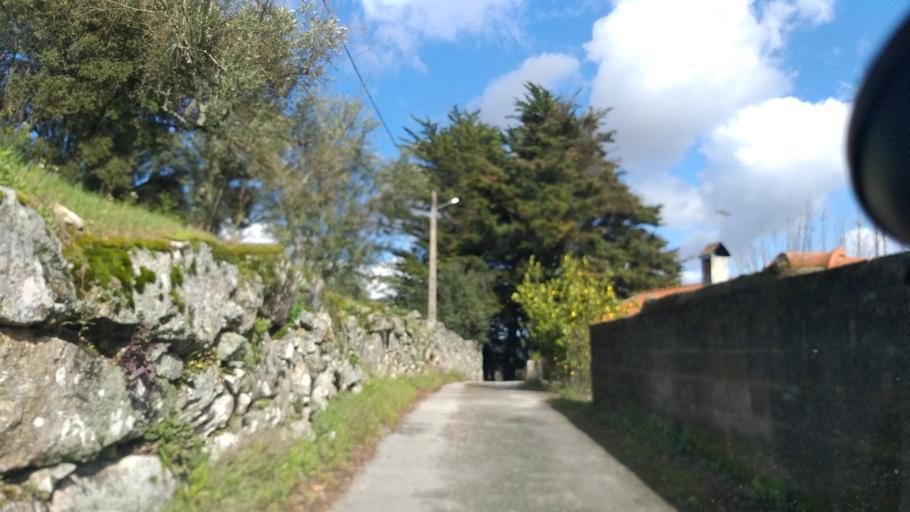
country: PT
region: Guarda
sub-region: Fornos de Algodres
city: Fornos de Algodres
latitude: 40.6178
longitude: -7.5442
